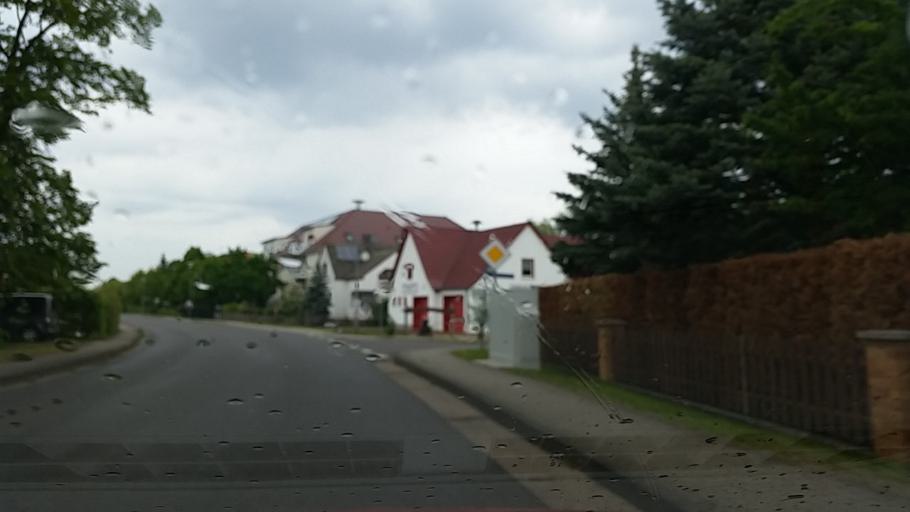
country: DE
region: Brandenburg
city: Spreenhagen
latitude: 52.3438
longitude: 13.8746
